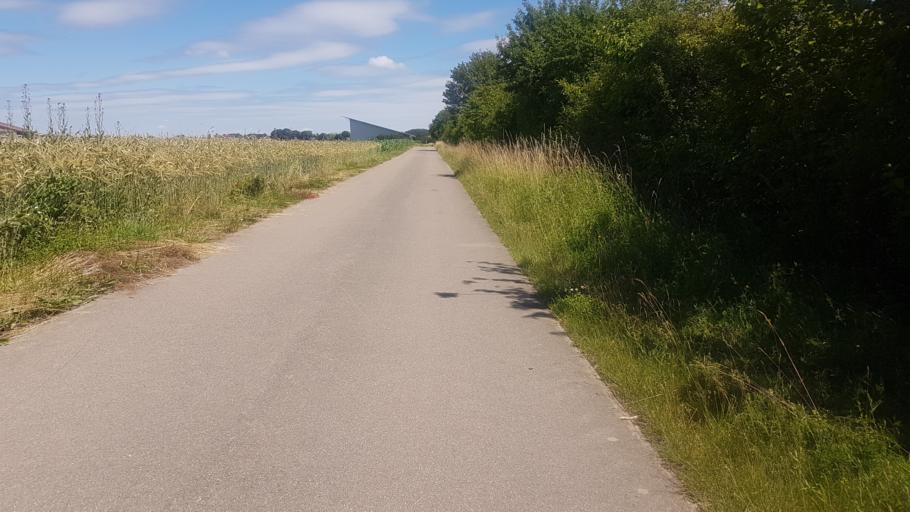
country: DE
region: Bavaria
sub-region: Swabia
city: Blindheim
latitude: 48.6356
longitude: 10.6296
